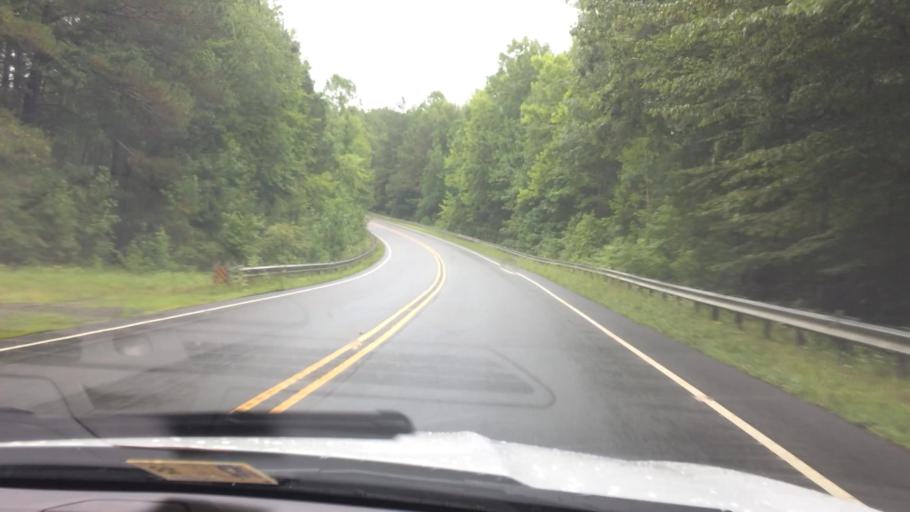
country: US
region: Virginia
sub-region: King William County
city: West Point
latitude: 37.5587
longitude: -76.7451
